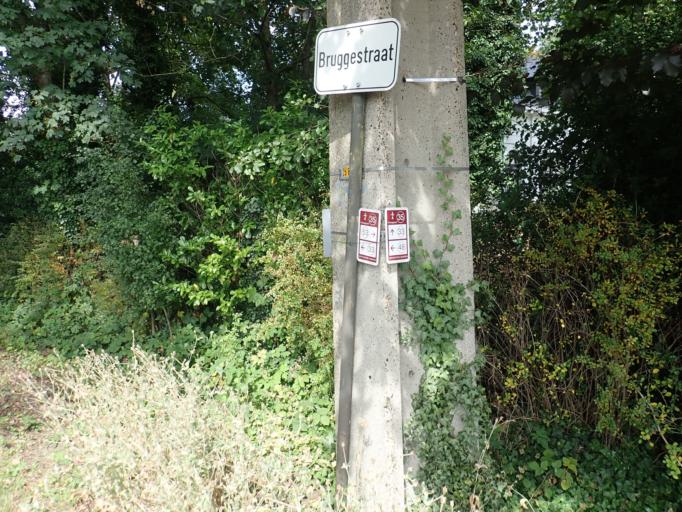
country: BE
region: Flanders
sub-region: Provincie Antwerpen
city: Zandhoven
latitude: 51.2070
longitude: 4.6662
